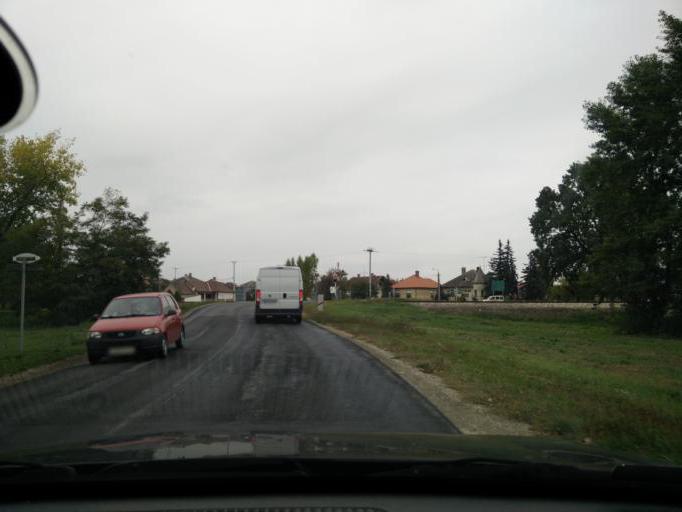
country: HU
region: Komarom-Esztergom
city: Tat
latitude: 47.7390
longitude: 18.6519
